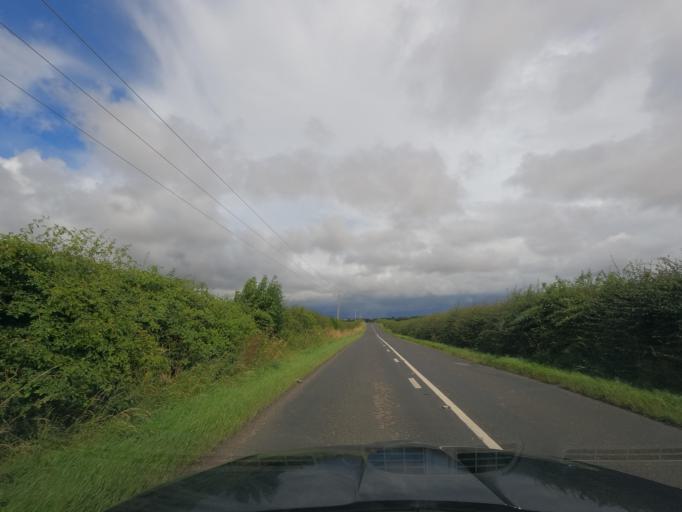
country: GB
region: England
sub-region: Northumberland
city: Ancroft
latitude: 55.6720
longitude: -2.0010
